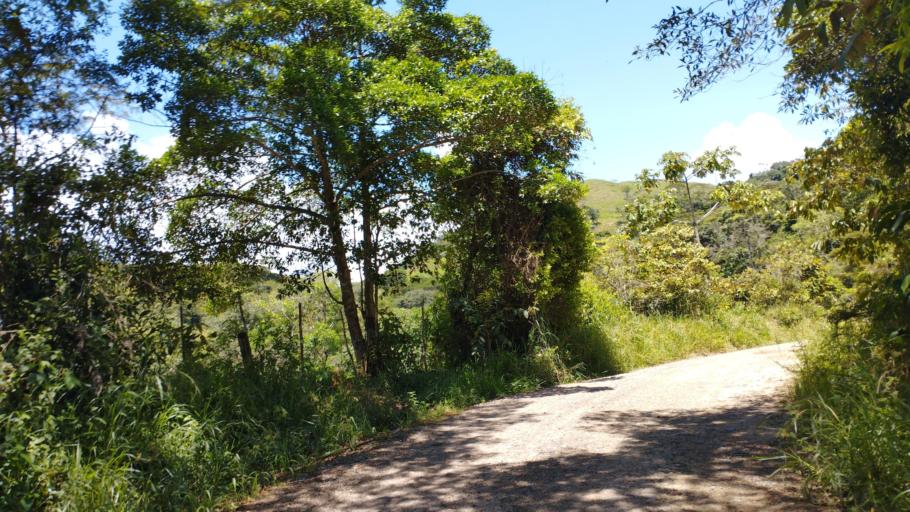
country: CO
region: Boyaca
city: San Luis de Gaceno
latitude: 4.7945
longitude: -73.1112
